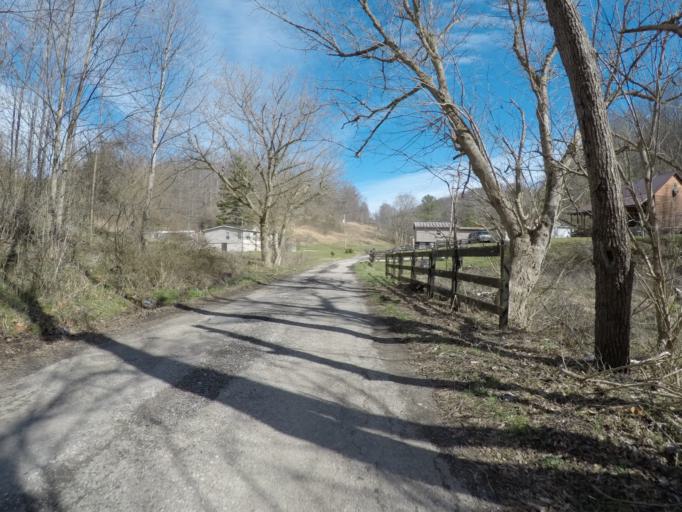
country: US
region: West Virginia
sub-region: Wayne County
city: Ceredo
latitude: 38.3482
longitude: -82.5566
